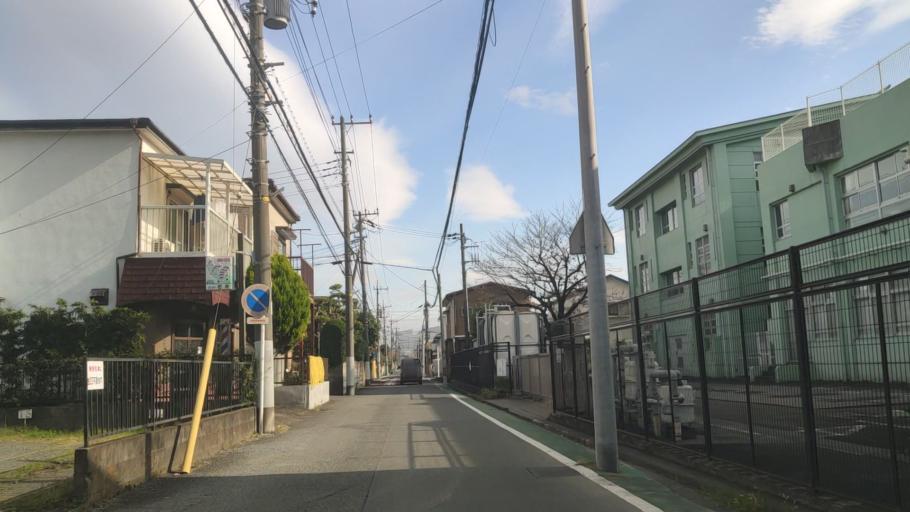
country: JP
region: Kanagawa
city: Atsugi
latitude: 35.4341
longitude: 139.3617
